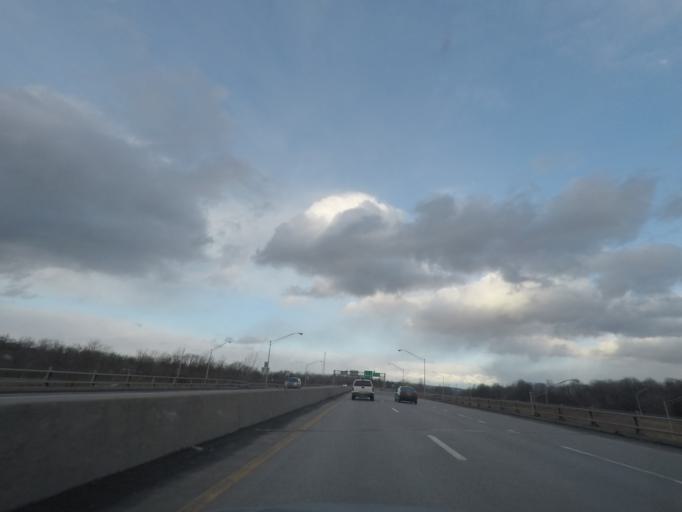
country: US
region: New York
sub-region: Oneida County
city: New Hartford
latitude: 43.0881
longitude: -75.2766
